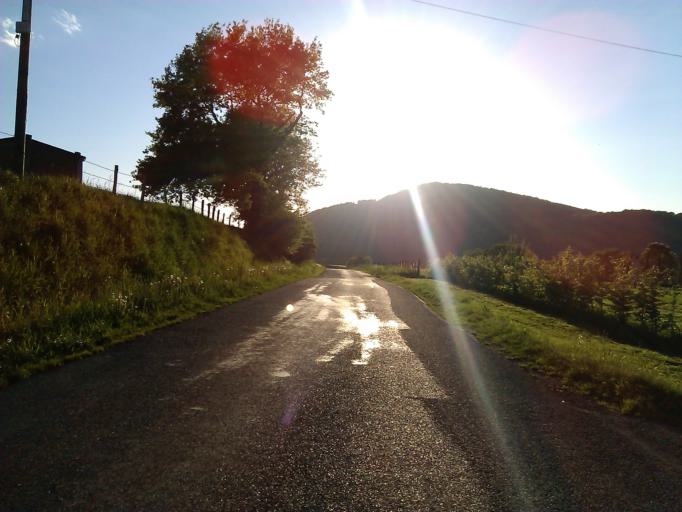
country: FR
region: Franche-Comte
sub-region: Departement du Doubs
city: Clerval
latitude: 47.3676
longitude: 6.4736
